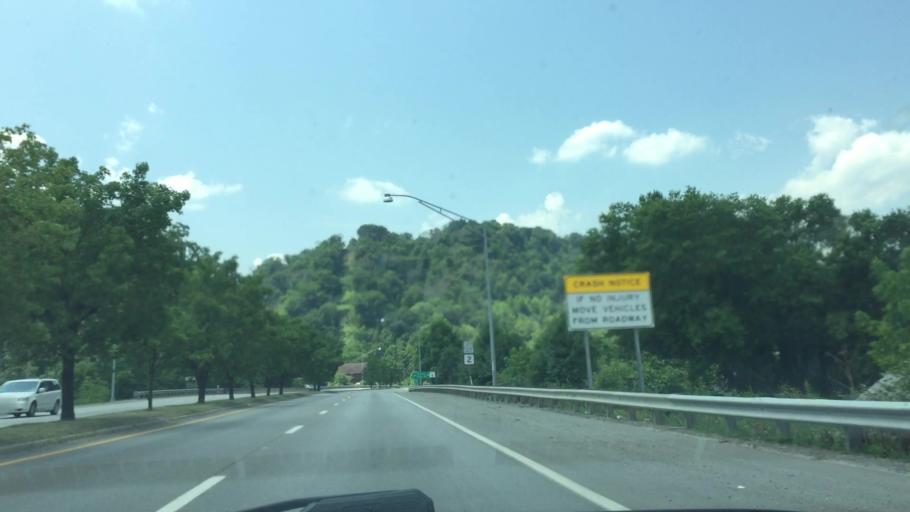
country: US
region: West Virginia
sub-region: Marshall County
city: Moundsville
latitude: 39.9064
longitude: -80.7556
